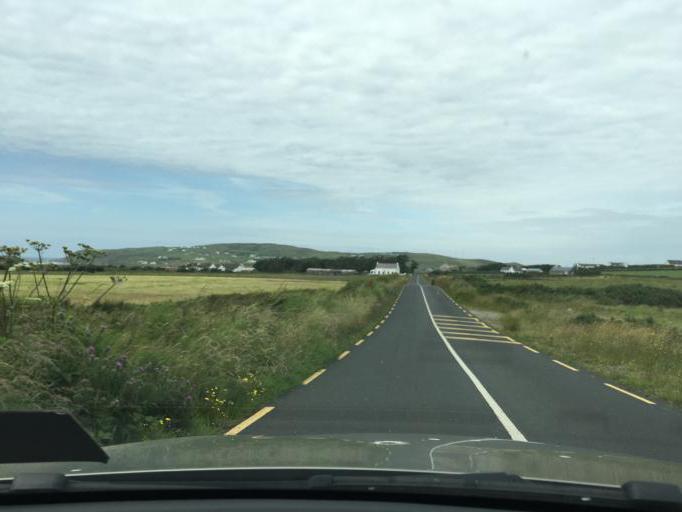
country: IE
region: Ulster
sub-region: County Donegal
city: Carndonagh
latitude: 55.3553
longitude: -7.3269
